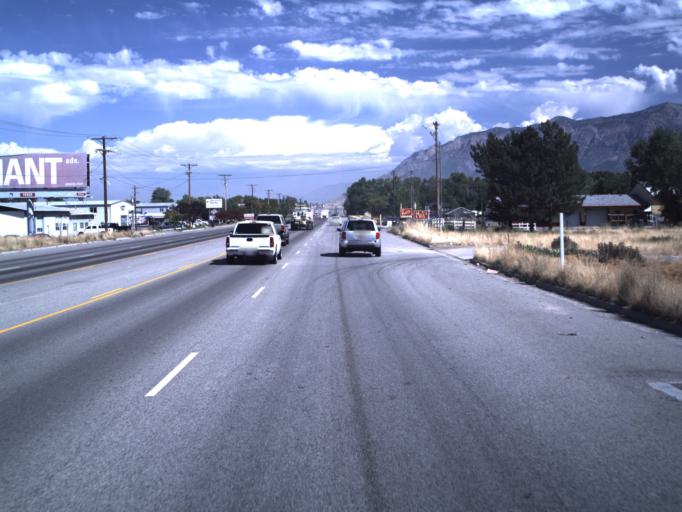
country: US
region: Utah
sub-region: Weber County
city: Marriott-Slaterville
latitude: 41.2355
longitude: -112.0254
